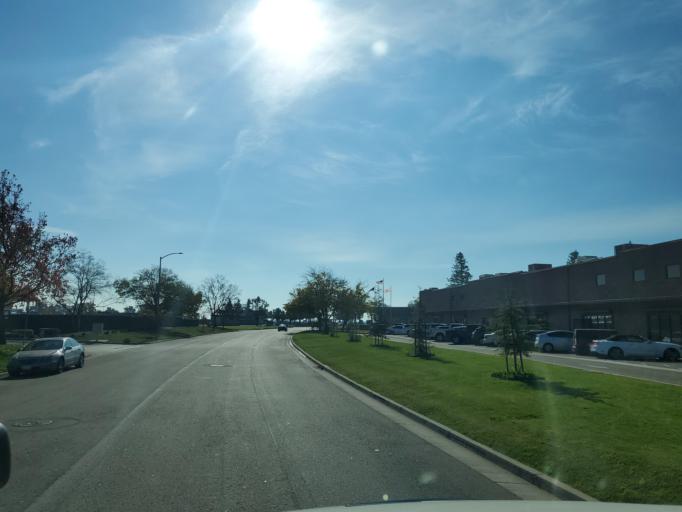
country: US
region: California
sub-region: San Joaquin County
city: Kennedy
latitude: 37.9080
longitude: -121.2286
